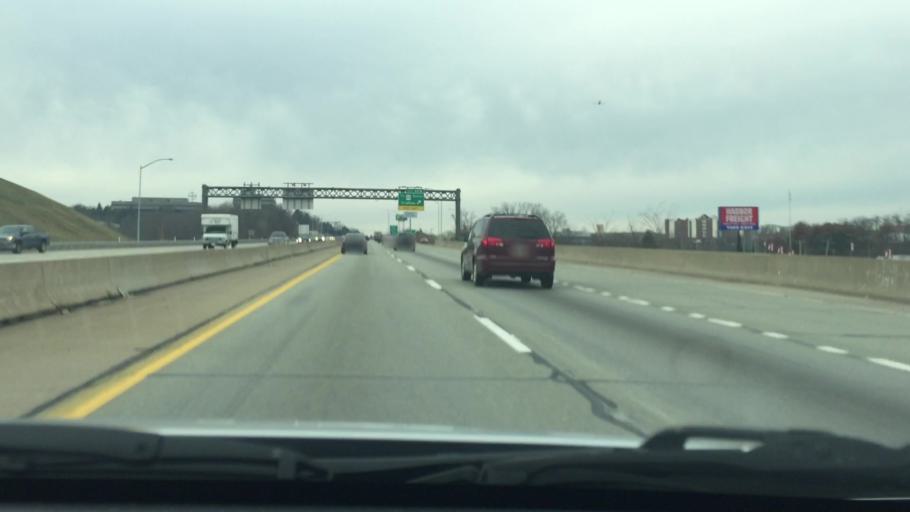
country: US
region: Pennsylvania
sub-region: Allegheny County
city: Rennerdale
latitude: 40.4406
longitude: -80.1559
